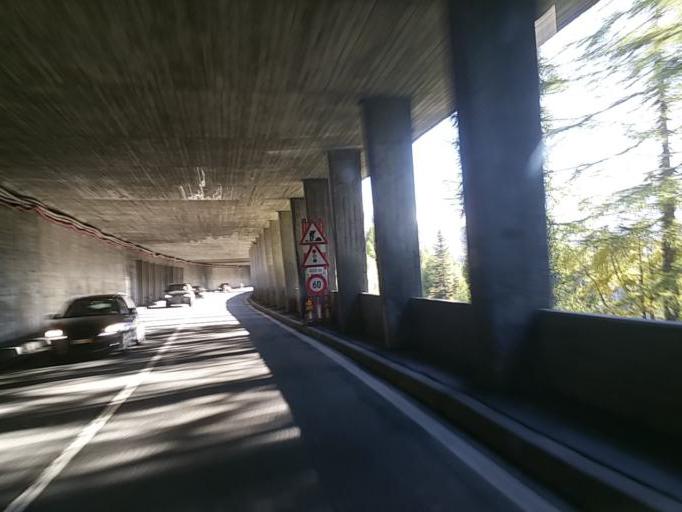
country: CH
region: Valais
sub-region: Brig District
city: Brig
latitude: 46.2673
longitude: 8.0402
